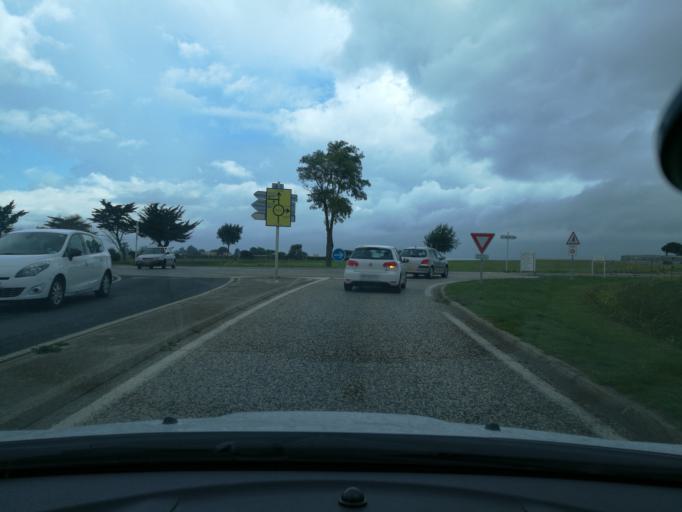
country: FR
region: Poitou-Charentes
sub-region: Departement de la Charente-Maritime
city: Saint-Martin-de-Re
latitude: 46.2008
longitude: -1.3744
